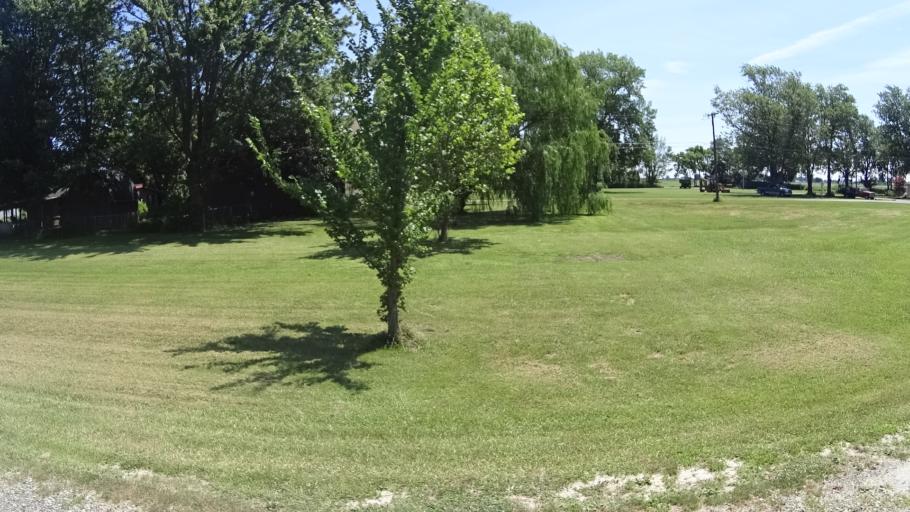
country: US
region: Ohio
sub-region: Ottawa County
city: Port Clinton
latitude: 41.4473
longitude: -82.8404
